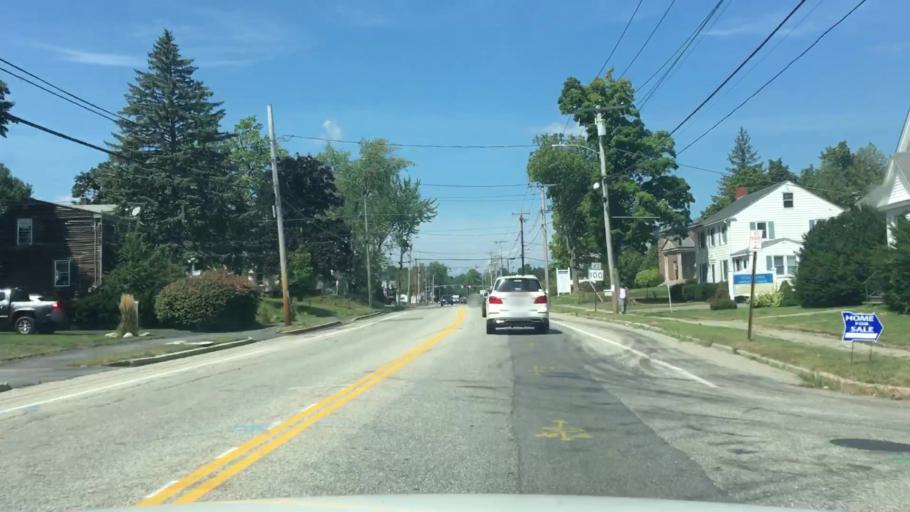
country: US
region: Maine
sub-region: Cumberland County
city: Portland
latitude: 43.6971
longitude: -70.2858
